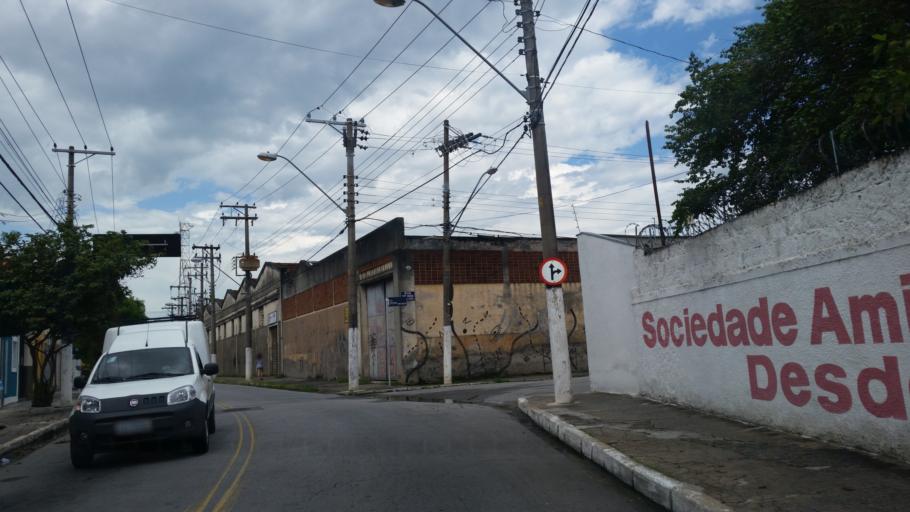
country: BR
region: Sao Paulo
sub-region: Taubate
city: Taubate
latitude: -23.0214
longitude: -45.5615
